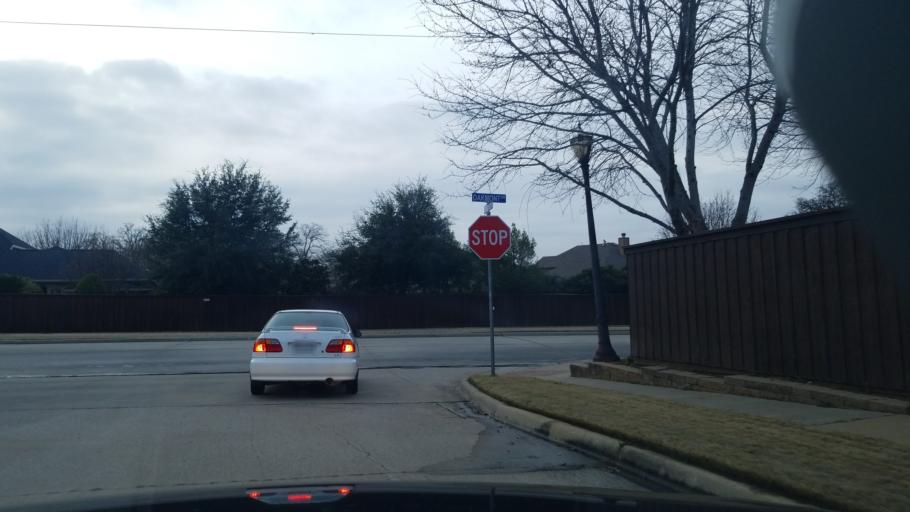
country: US
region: Texas
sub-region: Denton County
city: Corinth
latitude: 33.1363
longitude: -97.0892
